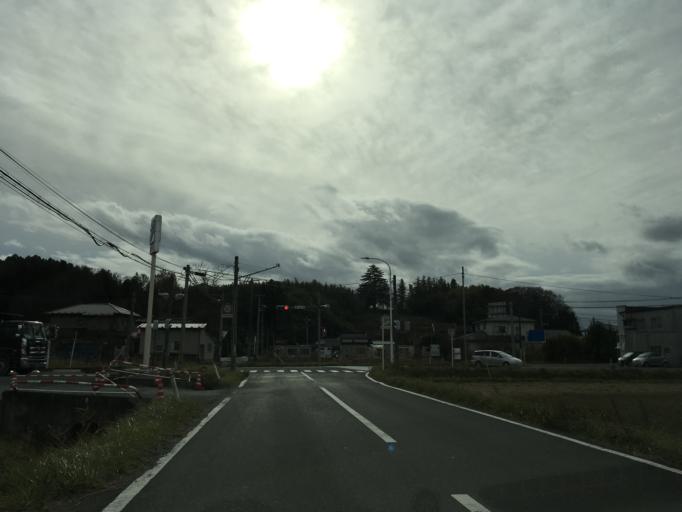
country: JP
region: Iwate
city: Ichinoseki
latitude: 38.7324
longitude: 141.2748
